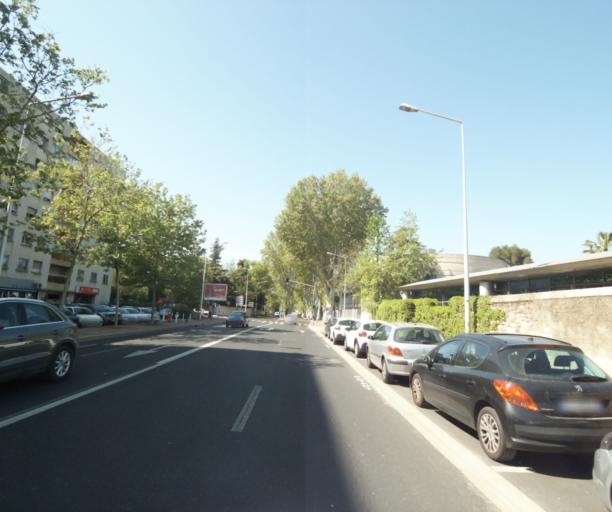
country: FR
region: Languedoc-Roussillon
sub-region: Departement de l'Herault
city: Montpellier
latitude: 43.6193
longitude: 3.8658
